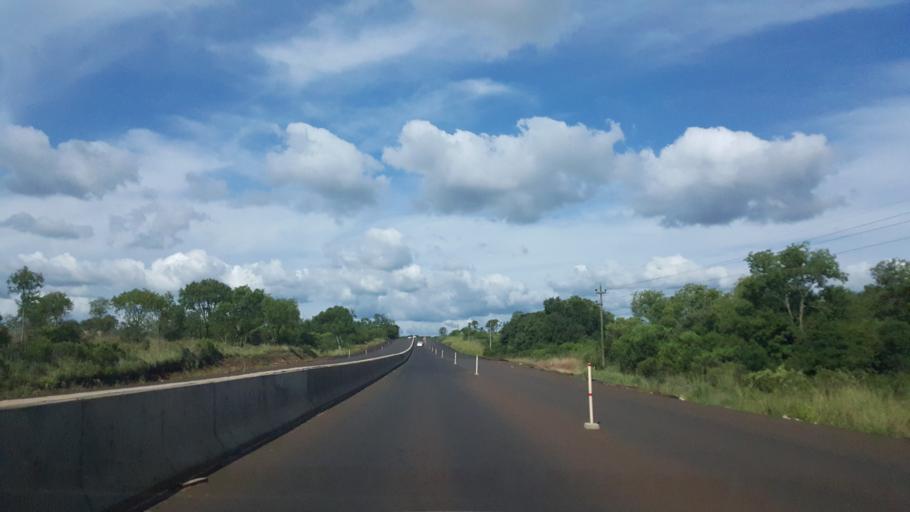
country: AR
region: Misiones
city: Santa Ana
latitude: -27.4265
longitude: -55.6258
